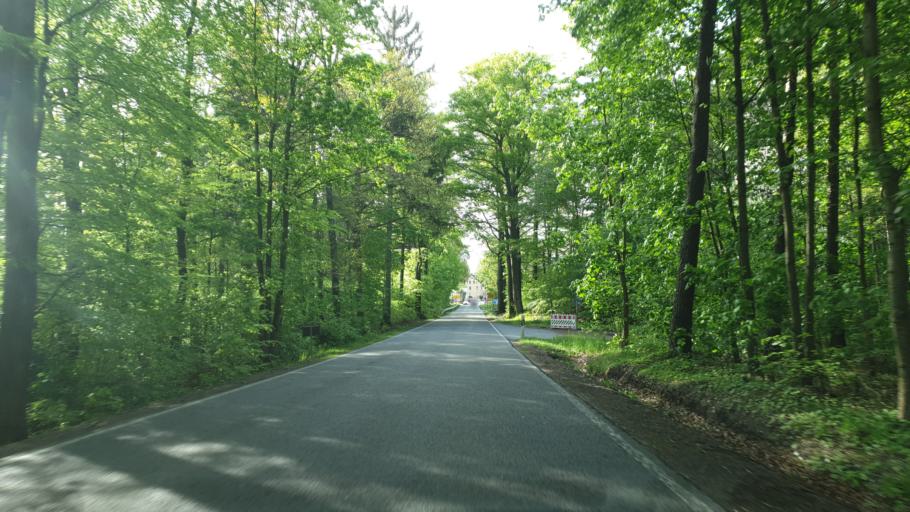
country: DE
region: Saxony
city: Lichtenstein
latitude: 50.7227
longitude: 12.6450
